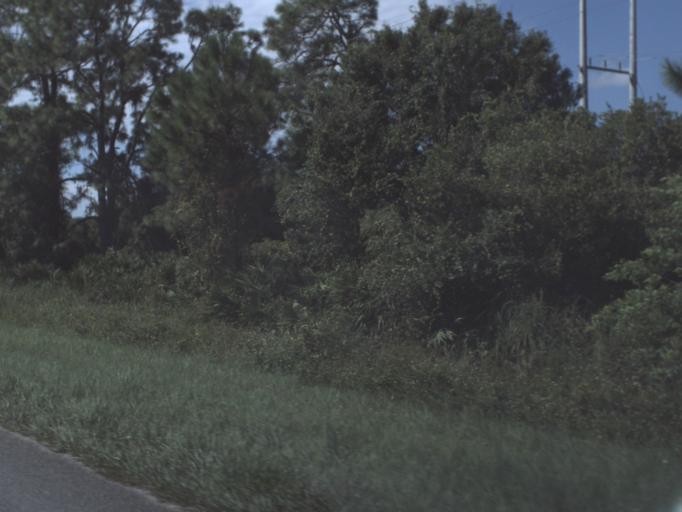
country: US
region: Florida
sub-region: Collier County
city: Immokalee
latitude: 26.3232
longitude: -81.3431
